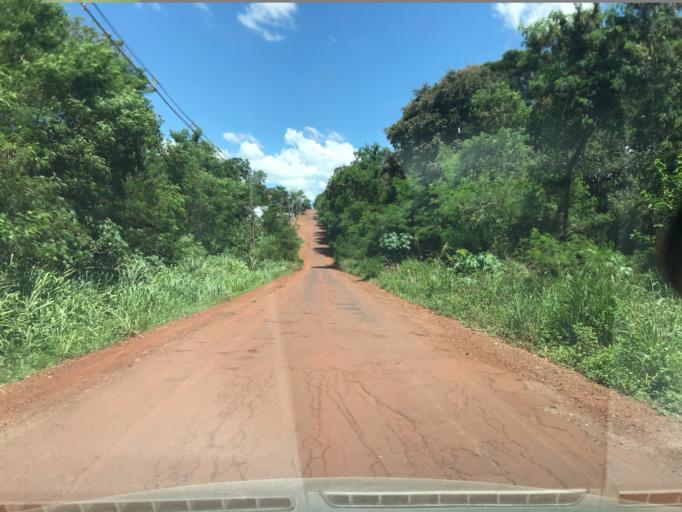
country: BR
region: Parana
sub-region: Palotina
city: Palotina
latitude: -24.2933
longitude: -53.8522
